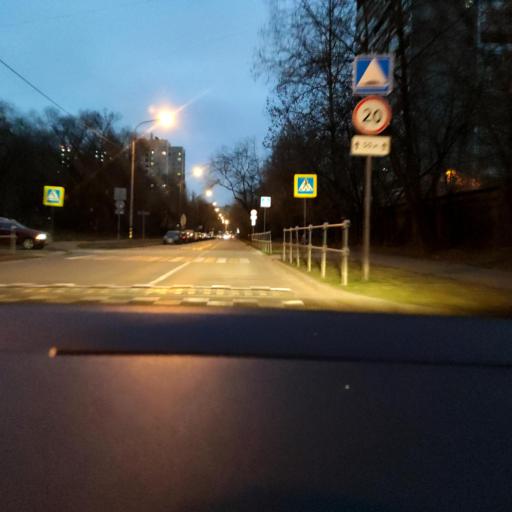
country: RU
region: Moscow
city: Gol'yanovo
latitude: 55.8153
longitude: 37.8206
